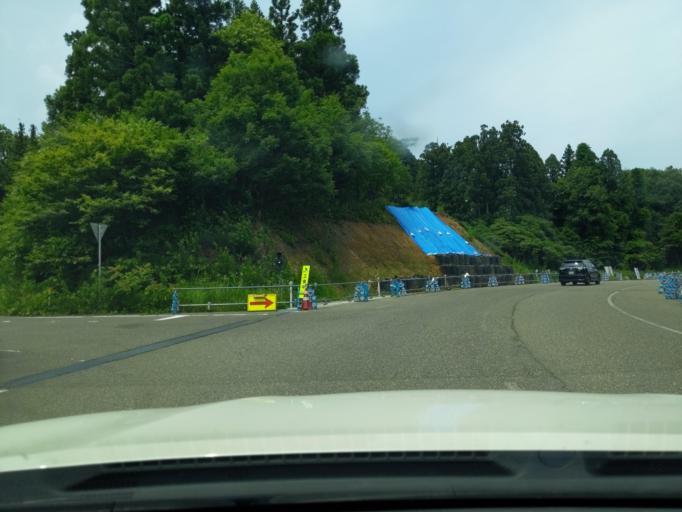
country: JP
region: Niigata
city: Kashiwazaki
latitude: 37.3474
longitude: 138.5503
